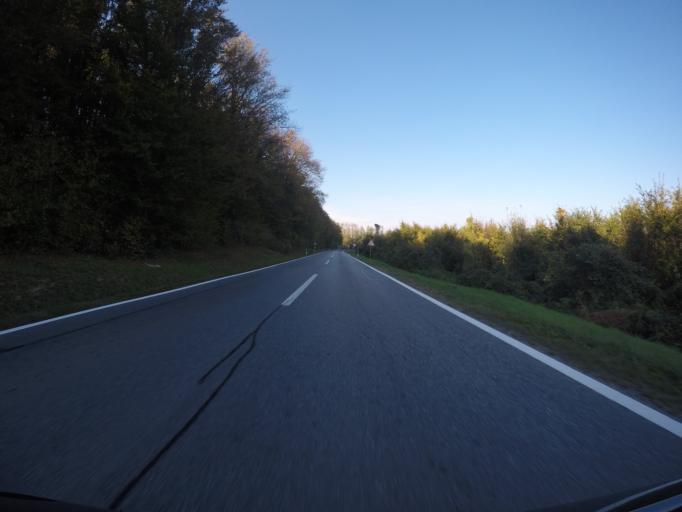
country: HR
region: Bjelovarsko-Bilogorska
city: Bjelovar
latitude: 45.9606
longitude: 16.8922
